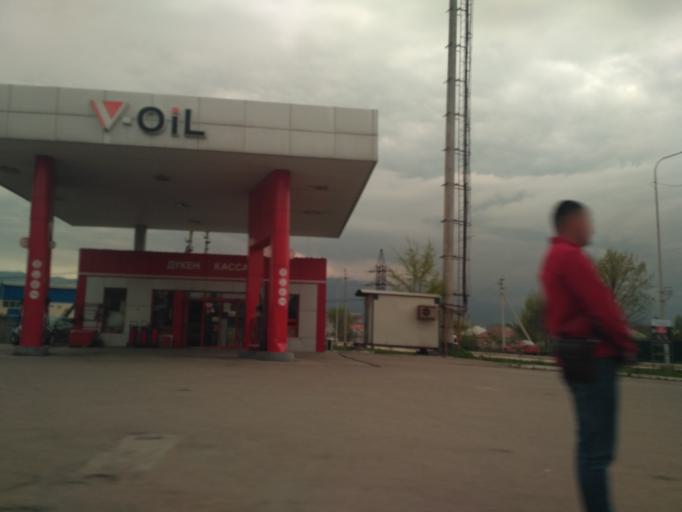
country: KZ
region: Almaty Oblysy
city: Burunday
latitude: 43.2106
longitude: 76.3296
